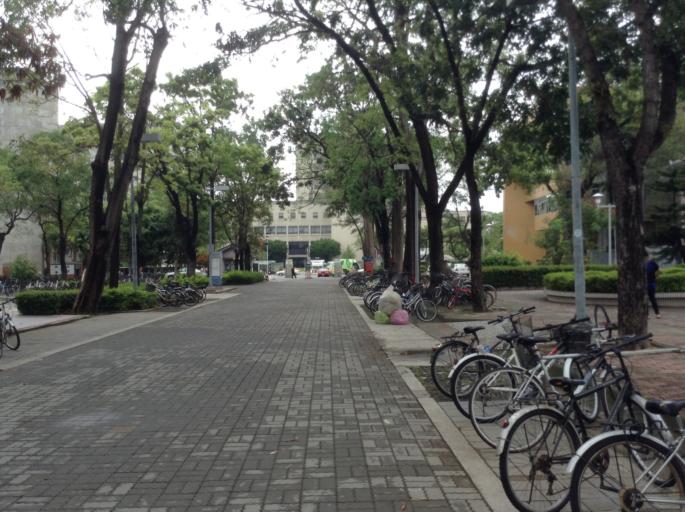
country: TW
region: Taiwan
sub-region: Tainan
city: Tainan
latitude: 22.9998
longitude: 120.2206
